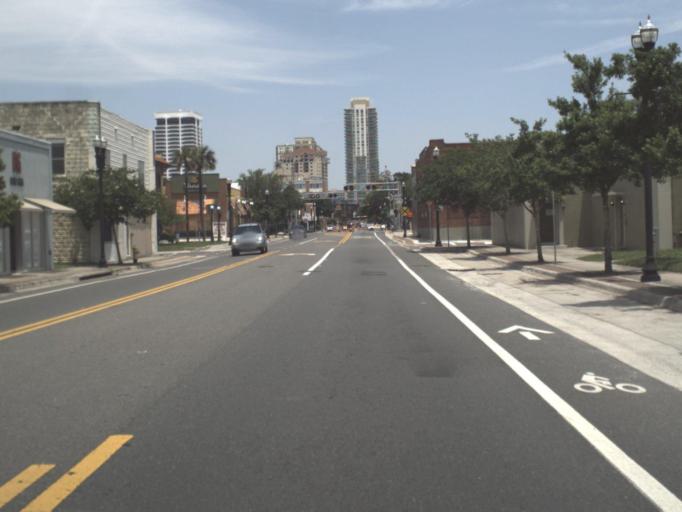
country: US
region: Florida
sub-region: Duval County
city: Jacksonville
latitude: 30.3099
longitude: -81.6547
